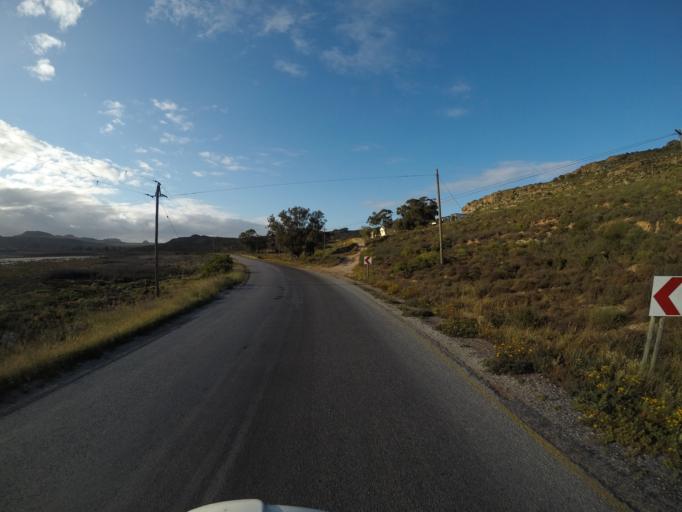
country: ZA
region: Western Cape
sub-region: West Coast District Municipality
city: Clanwilliam
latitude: -32.3204
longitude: 18.3578
